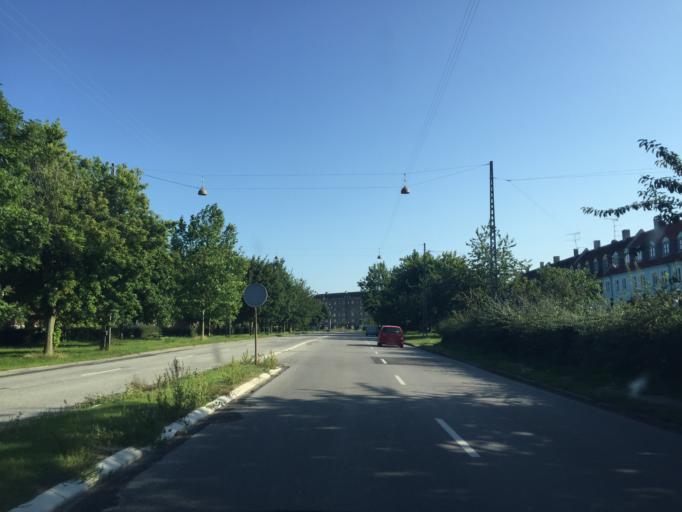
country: DK
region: Capital Region
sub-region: Kobenhavn
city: Copenhagen
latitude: 55.7058
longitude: 12.5570
